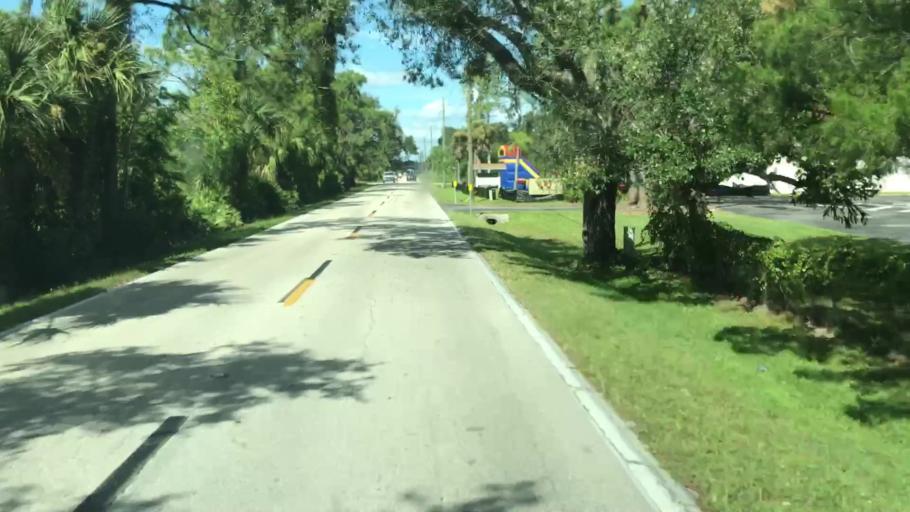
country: US
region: Florida
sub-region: Lee County
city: Alva
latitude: 26.7004
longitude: -81.6009
